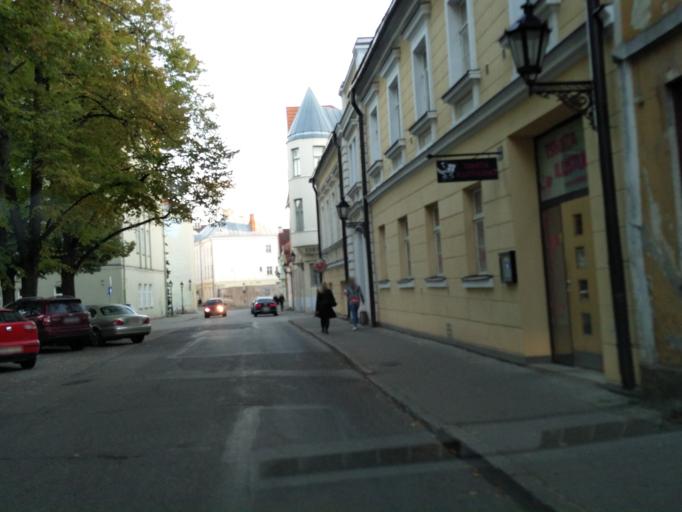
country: EE
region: Tartu
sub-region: Tartu linn
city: Tartu
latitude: 58.3822
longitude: 26.7227
